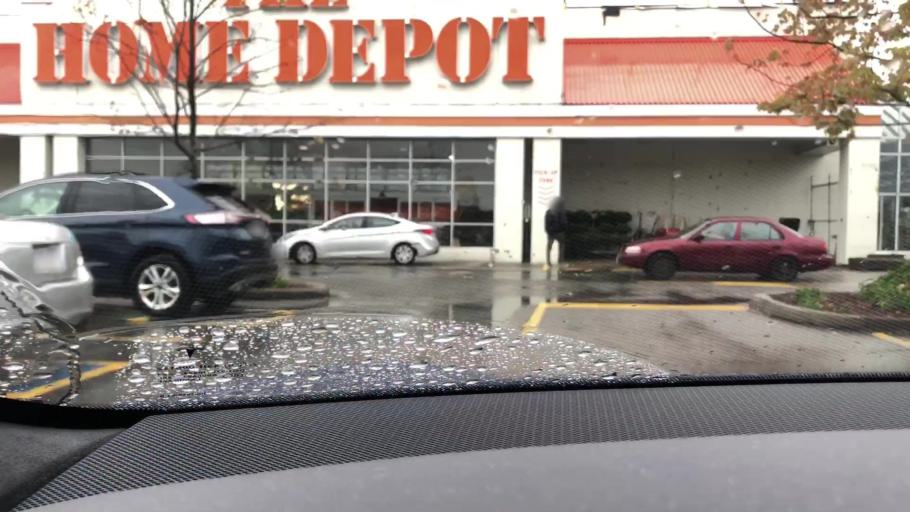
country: CA
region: British Columbia
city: Port Moody
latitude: 49.2281
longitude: -122.8421
